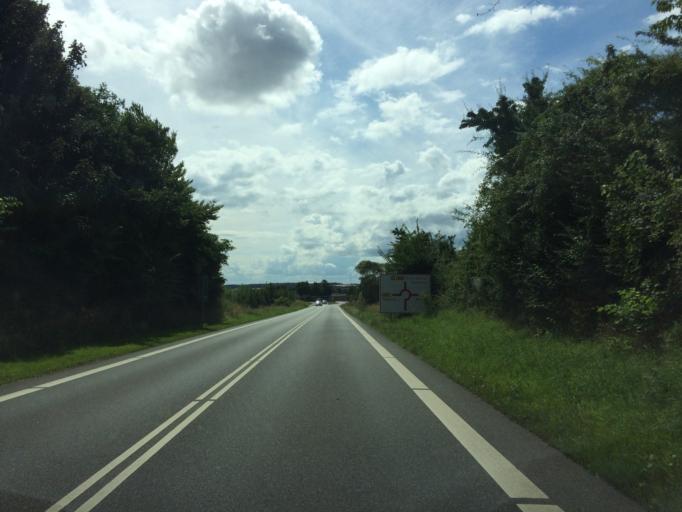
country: DK
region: South Denmark
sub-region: Faaborg-Midtfyn Kommune
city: Faaborg
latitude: 55.1152
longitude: 10.2435
